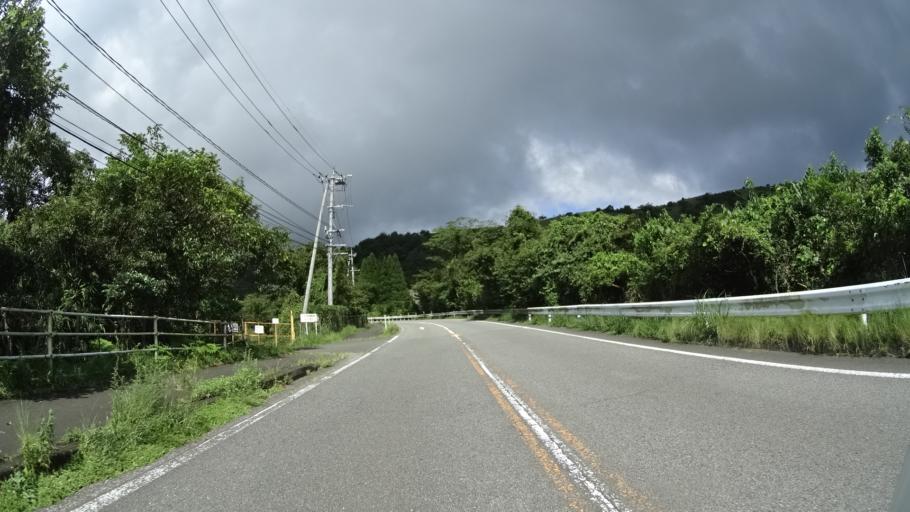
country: JP
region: Oita
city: Beppu
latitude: 33.3496
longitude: 131.4388
